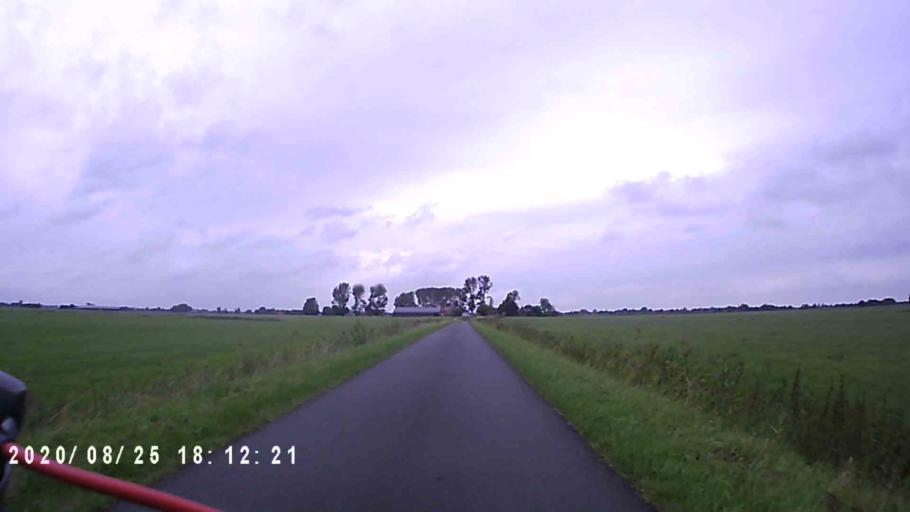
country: NL
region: Groningen
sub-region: Gemeente Zuidhorn
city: Aduard
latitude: 53.2884
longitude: 6.4373
